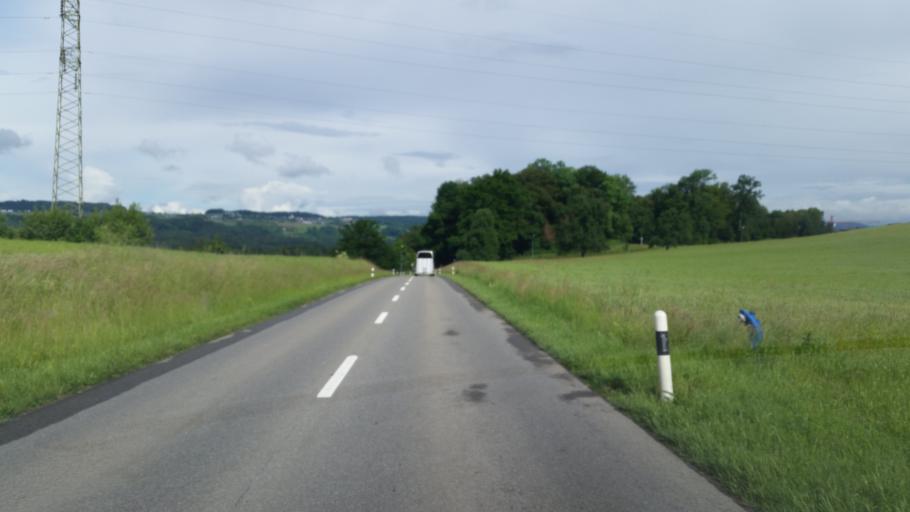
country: CH
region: Aargau
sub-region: Bezirk Bremgarten
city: Bremgarten
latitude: 47.3368
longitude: 8.3341
